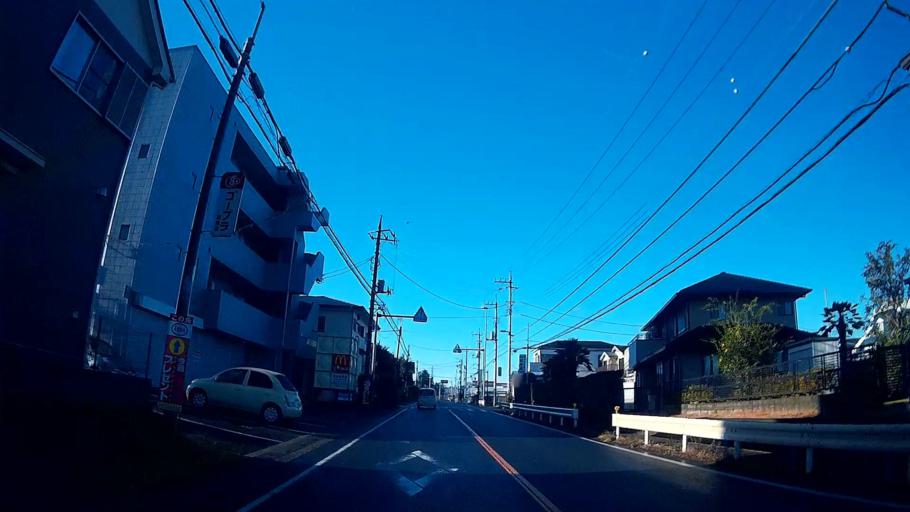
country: JP
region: Saitama
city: Sayama
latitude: 35.8489
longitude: 139.3712
